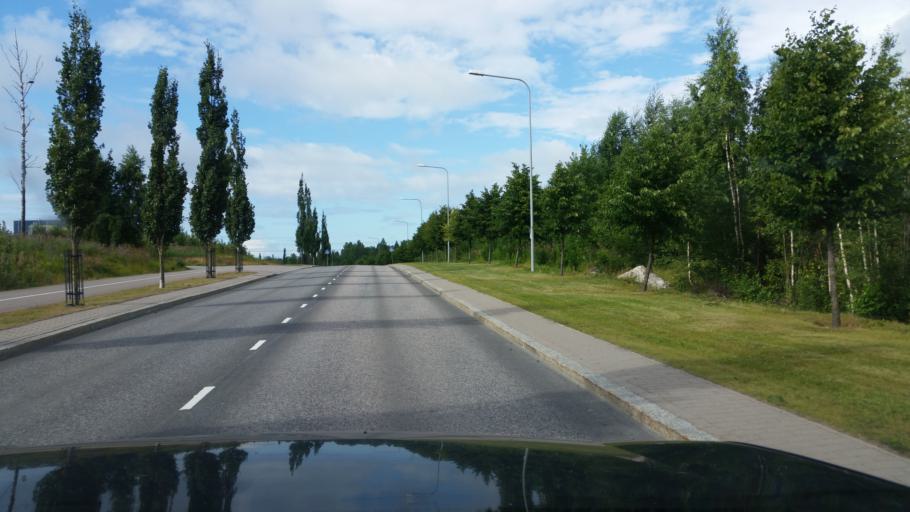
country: FI
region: Uusimaa
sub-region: Helsinki
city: Vantaa
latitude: 60.2240
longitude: 25.1640
